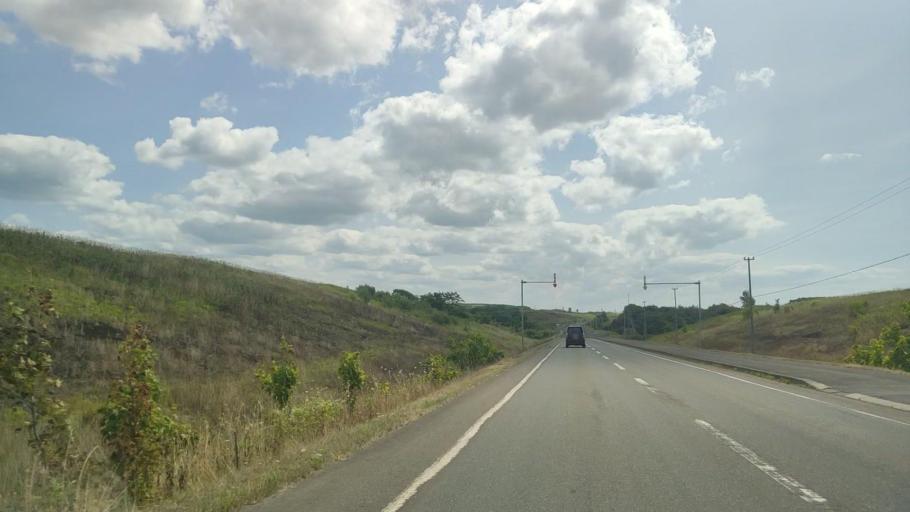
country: JP
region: Hokkaido
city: Makubetsu
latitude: 44.7964
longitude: 141.7887
